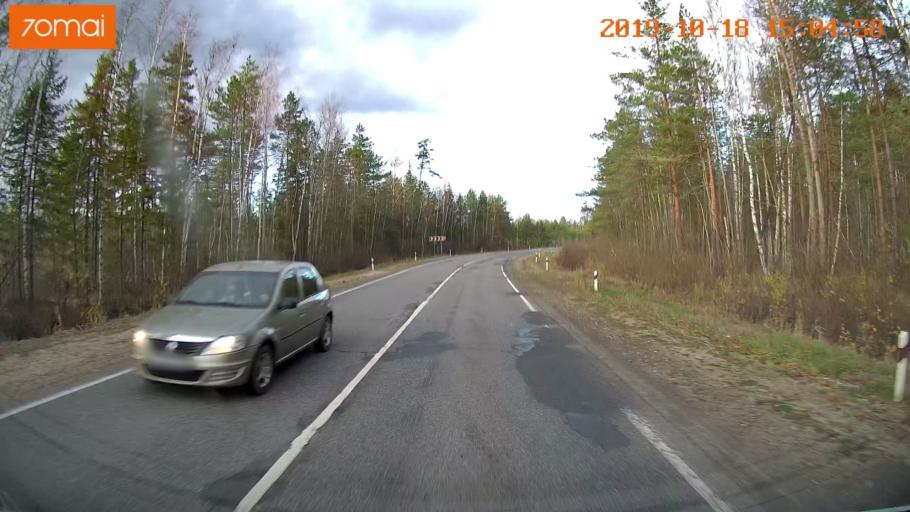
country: RU
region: Vladimir
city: Kurlovo
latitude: 55.5084
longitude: 40.5700
